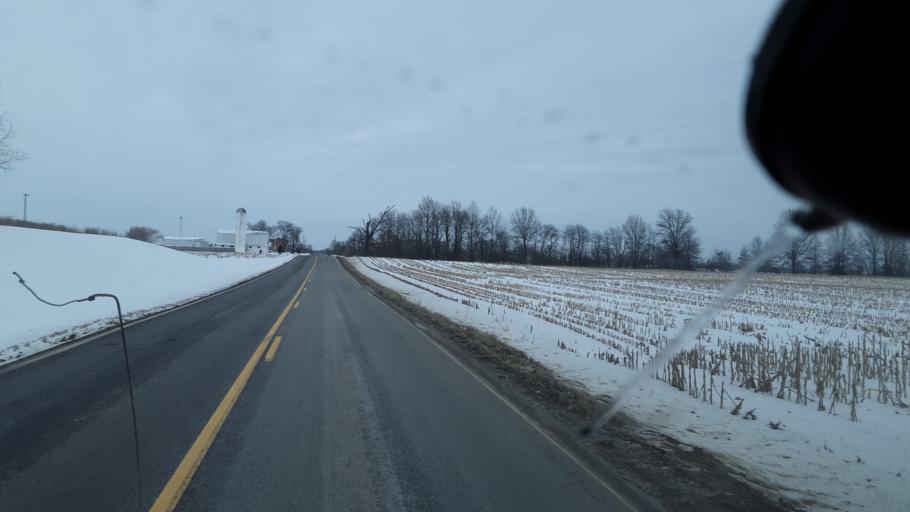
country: US
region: Ohio
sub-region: Union County
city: New California
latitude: 40.2150
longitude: -83.1888
